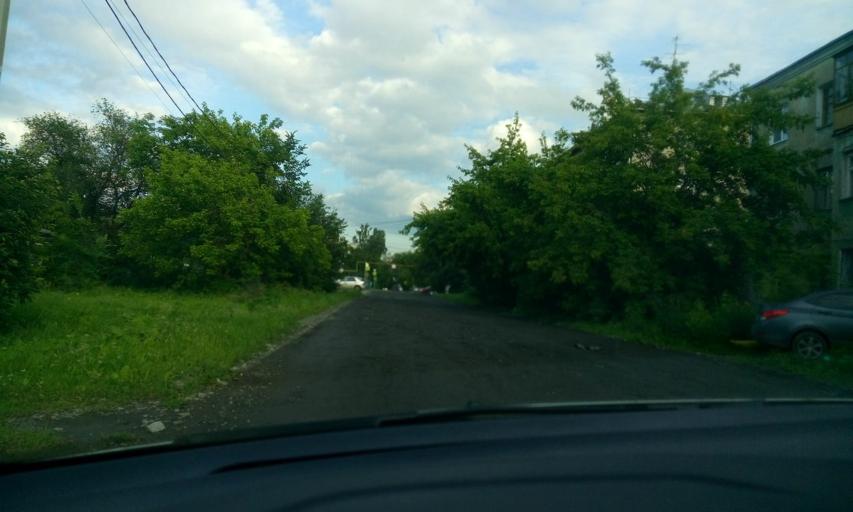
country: RU
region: Sverdlovsk
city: Yekaterinburg
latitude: 56.8887
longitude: 60.5642
